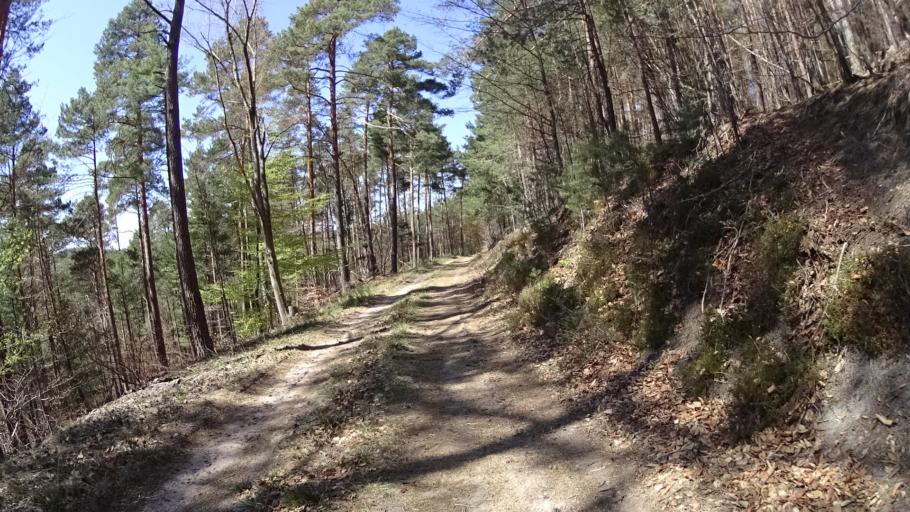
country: DE
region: Rheinland-Pfalz
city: Neidenfels
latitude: 49.4211
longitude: 8.0436
